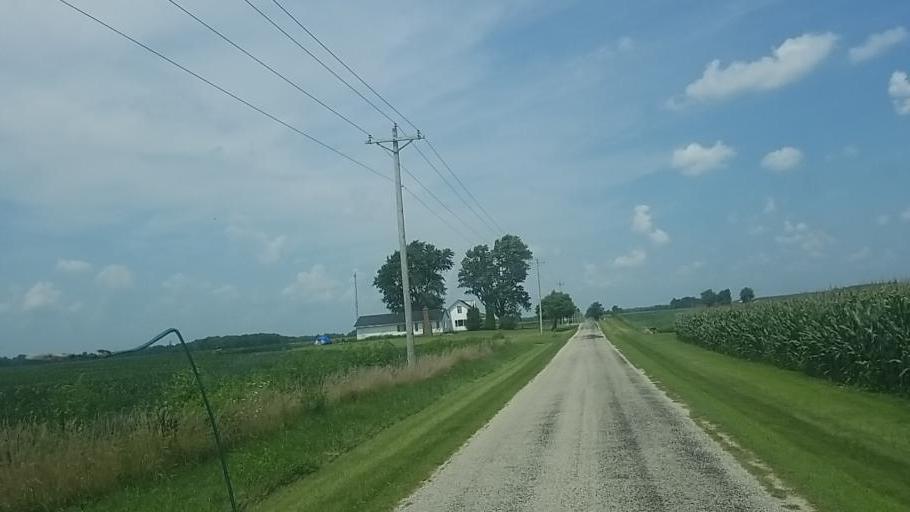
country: US
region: Ohio
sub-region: Union County
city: Richwood
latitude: 40.6140
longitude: -83.3617
